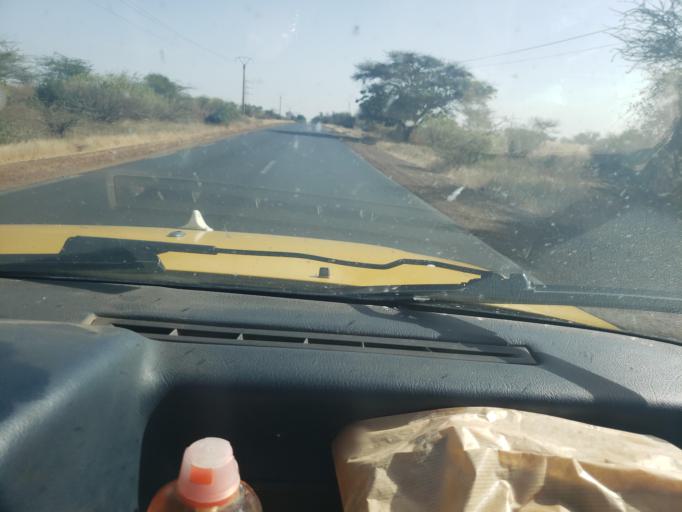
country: SN
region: Louga
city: Louga
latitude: 15.6587
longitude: -16.2572
